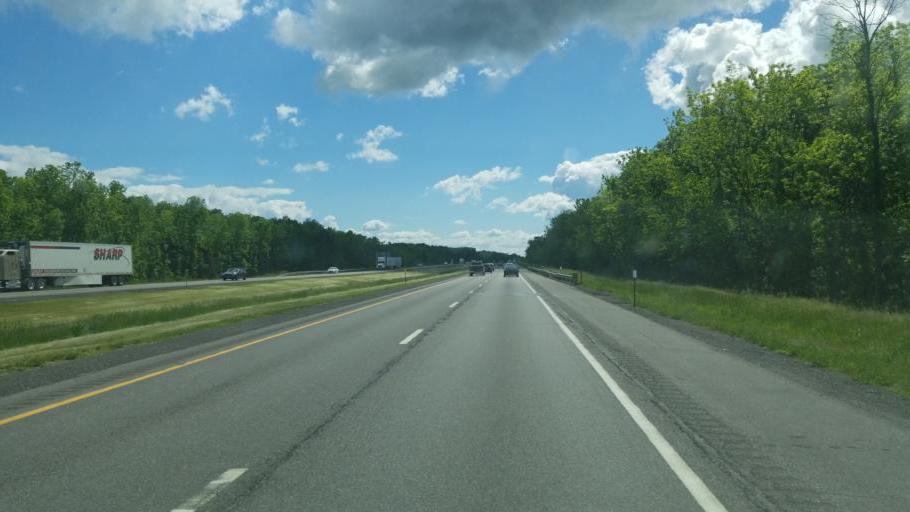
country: US
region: New York
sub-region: Madison County
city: Canastota
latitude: 43.0940
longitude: -75.8130
